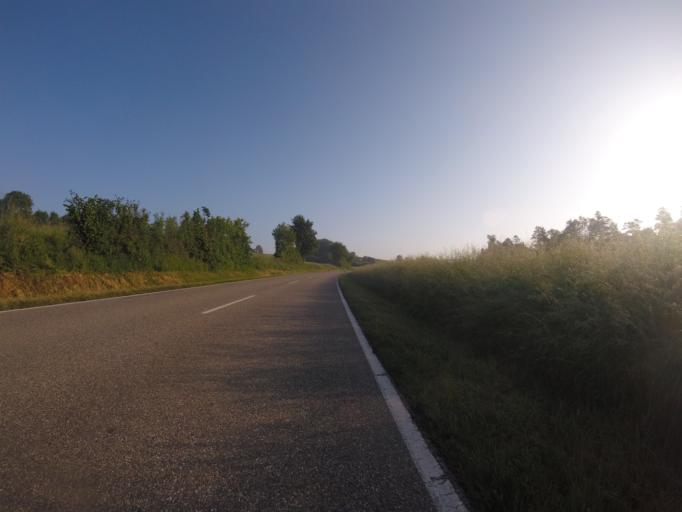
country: DE
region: Baden-Wuerttemberg
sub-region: Regierungsbezirk Stuttgart
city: Beilstein
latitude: 49.0496
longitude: 9.3094
